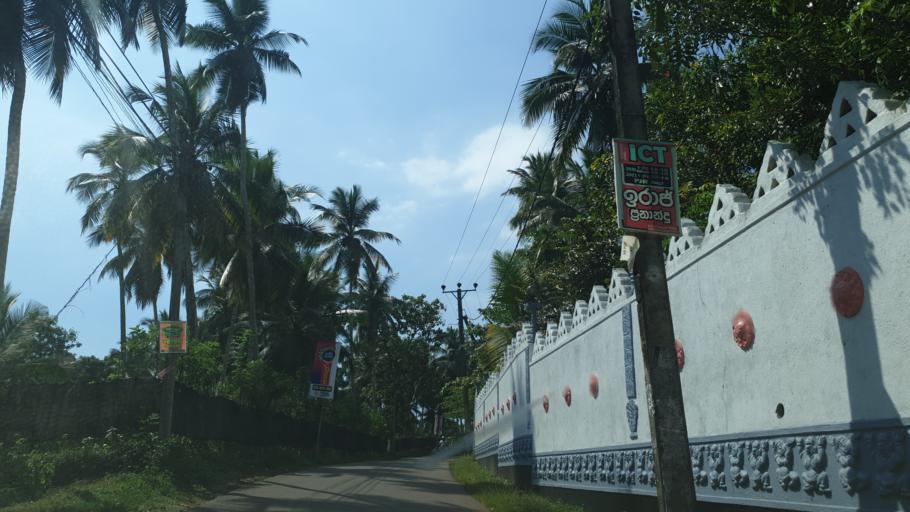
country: LK
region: Western
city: Panadura
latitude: 6.7228
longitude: 79.9564
